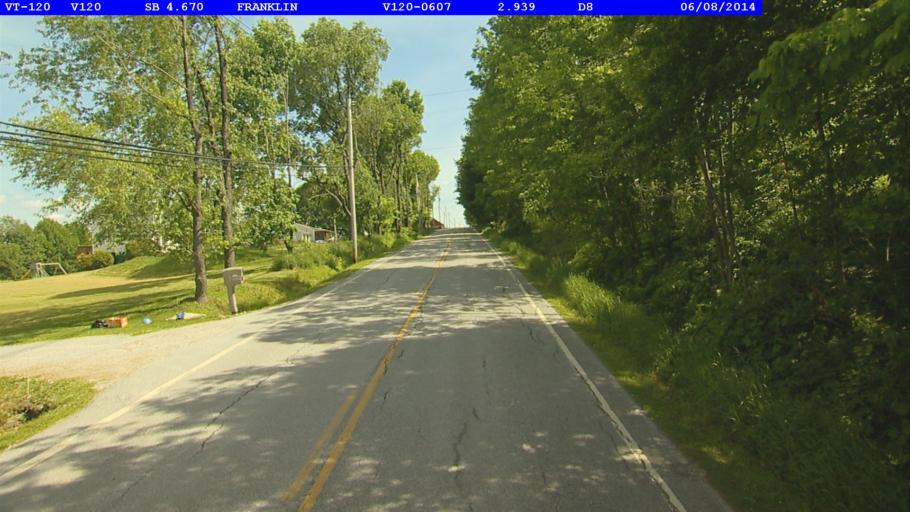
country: US
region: Vermont
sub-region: Franklin County
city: Enosburg Falls
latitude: 44.9748
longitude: -72.9120
